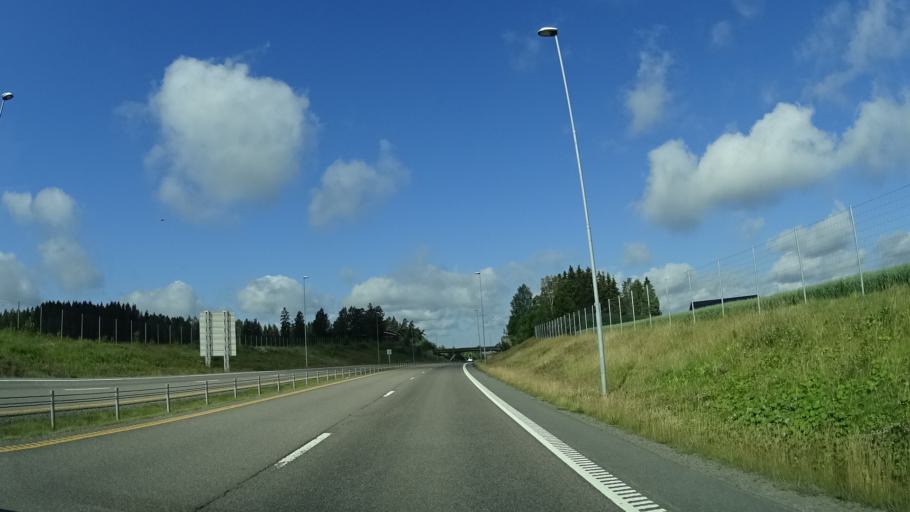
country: NO
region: Ostfold
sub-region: Askim
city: Askim
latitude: 59.5697
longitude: 11.2038
